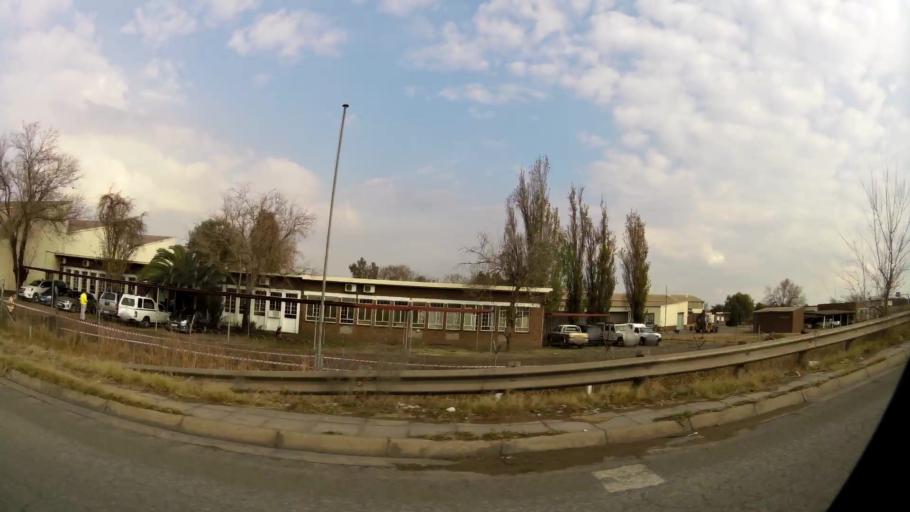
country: ZA
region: Gauteng
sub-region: Sedibeng District Municipality
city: Vereeniging
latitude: -26.6852
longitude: 27.9067
